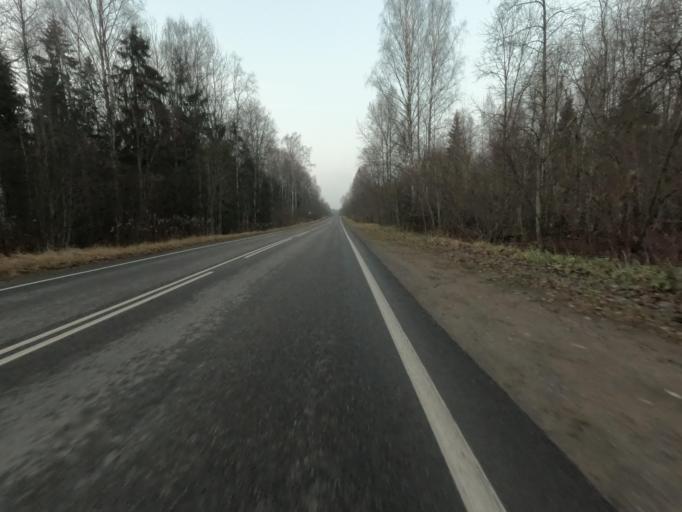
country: RU
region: Leningrad
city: Kirovsk
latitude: 59.8527
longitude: 30.9915
